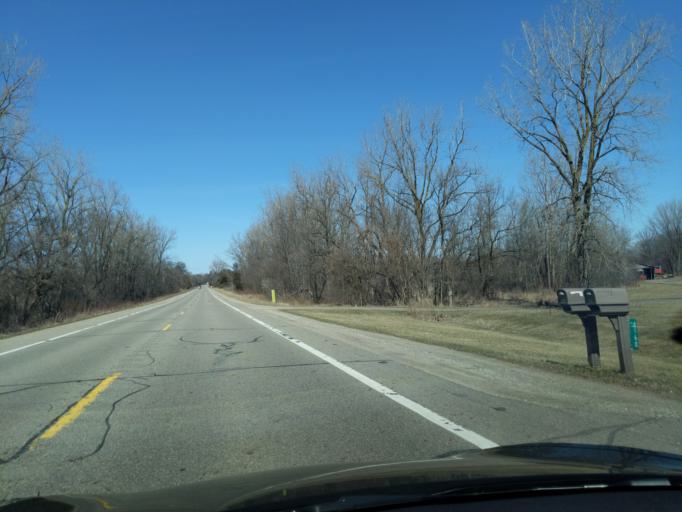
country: US
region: Michigan
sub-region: Ionia County
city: Lake Odessa
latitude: 42.7152
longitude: -85.0950
